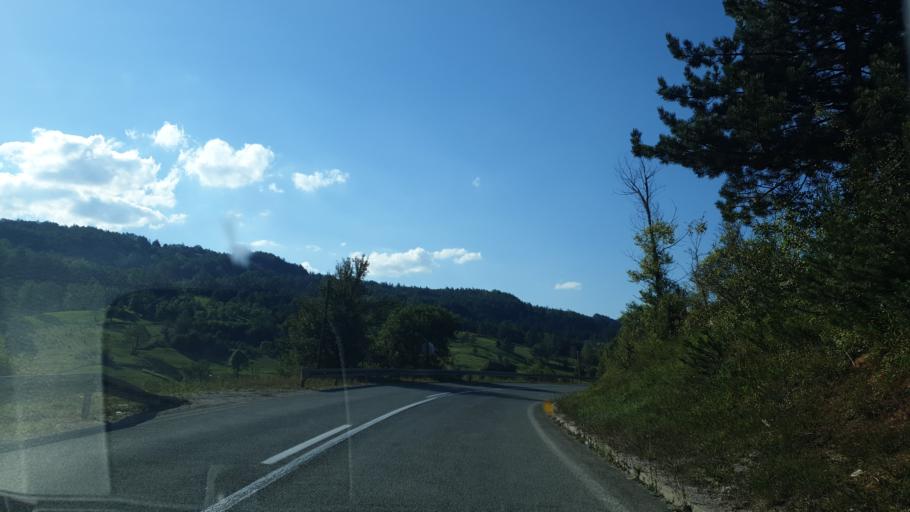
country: RS
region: Central Serbia
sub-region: Zlatiborski Okrug
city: Nova Varos
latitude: 43.5461
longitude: 19.7837
